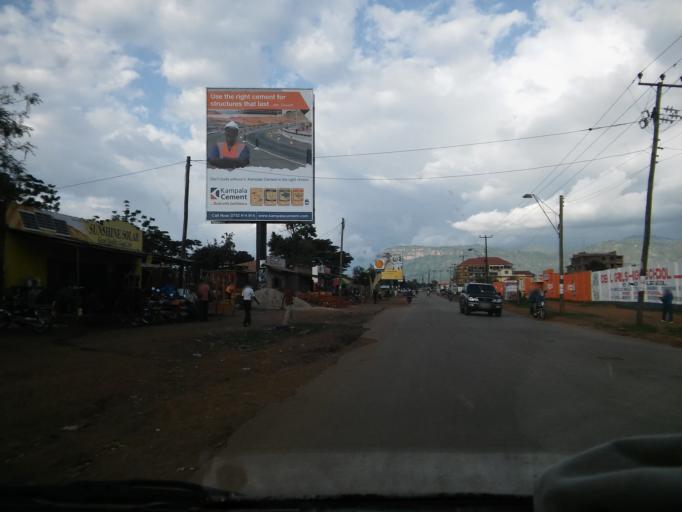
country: UG
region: Eastern Region
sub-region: Mbale District
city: Mbale
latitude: 1.0794
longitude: 34.1650
